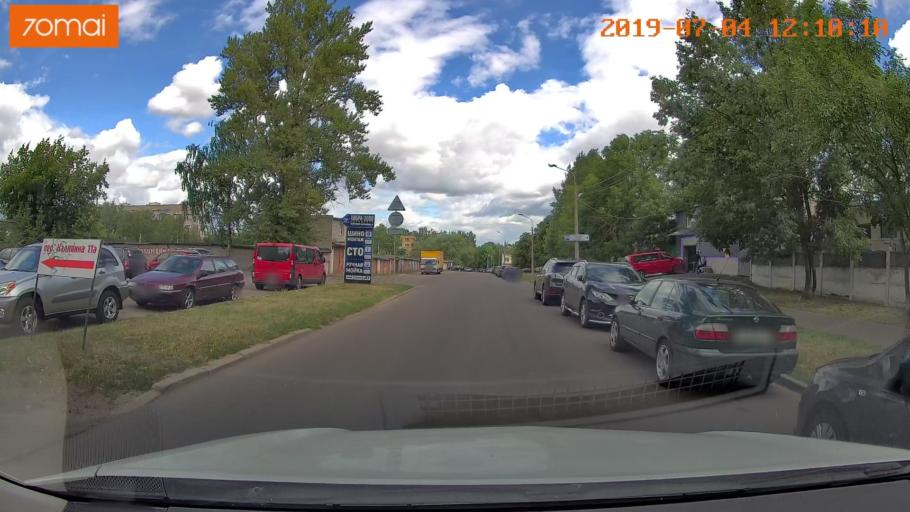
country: BY
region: Minsk
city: Minsk
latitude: 53.9315
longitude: 27.6072
